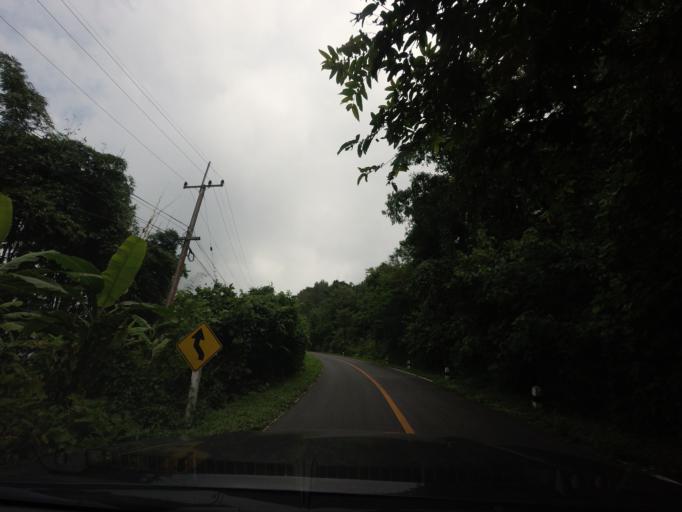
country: TH
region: Nan
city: Pua
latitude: 19.1881
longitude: 101.0210
